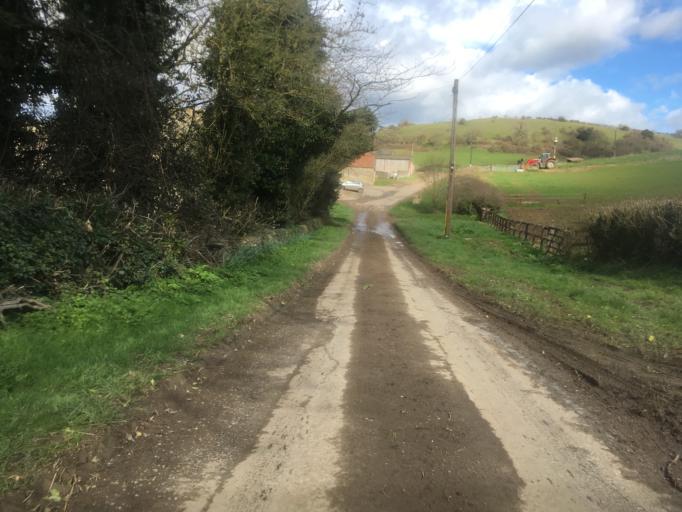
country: GB
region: England
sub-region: South Gloucestershire
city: Horton
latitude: 51.5704
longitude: -2.3386
